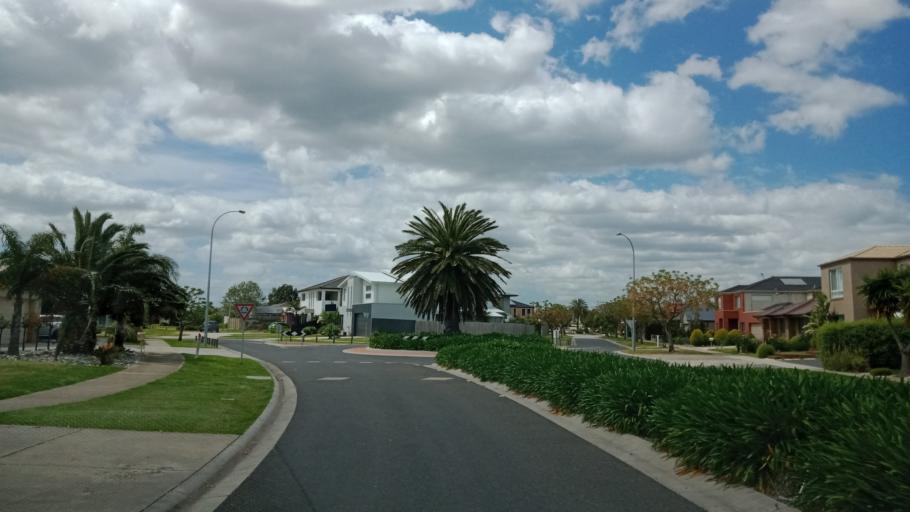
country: AU
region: Victoria
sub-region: Kingston
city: Patterson Lakes
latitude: -38.0592
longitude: 145.1395
